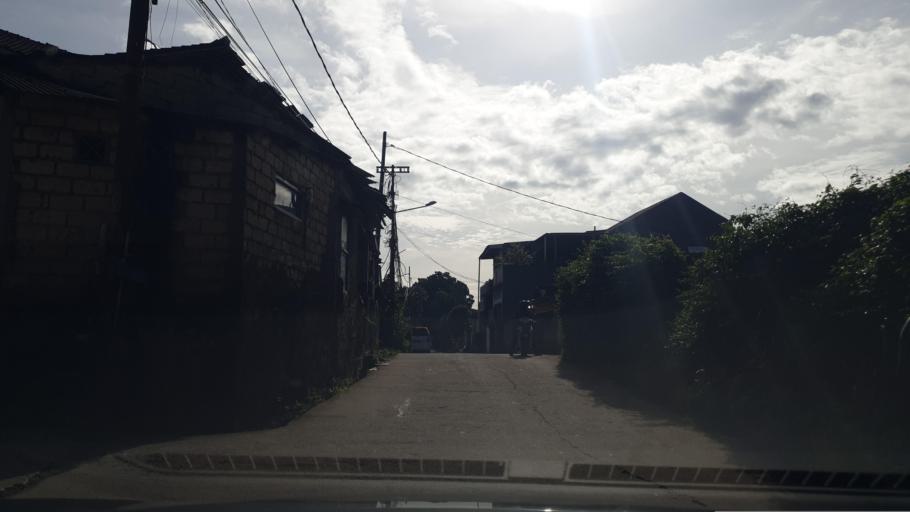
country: ID
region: West Java
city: Sawangan
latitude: -6.3579
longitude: 106.7812
